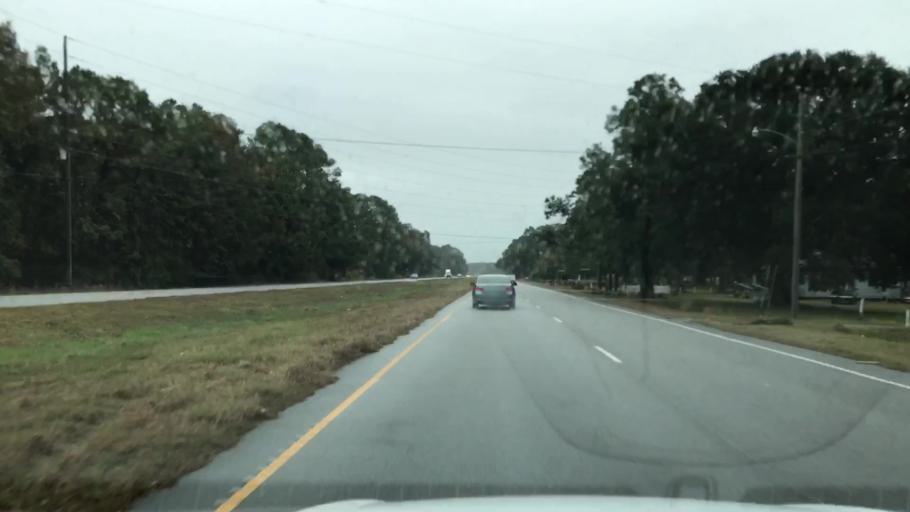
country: US
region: South Carolina
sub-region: Charleston County
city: Isle of Palms
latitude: 32.8918
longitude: -79.7390
